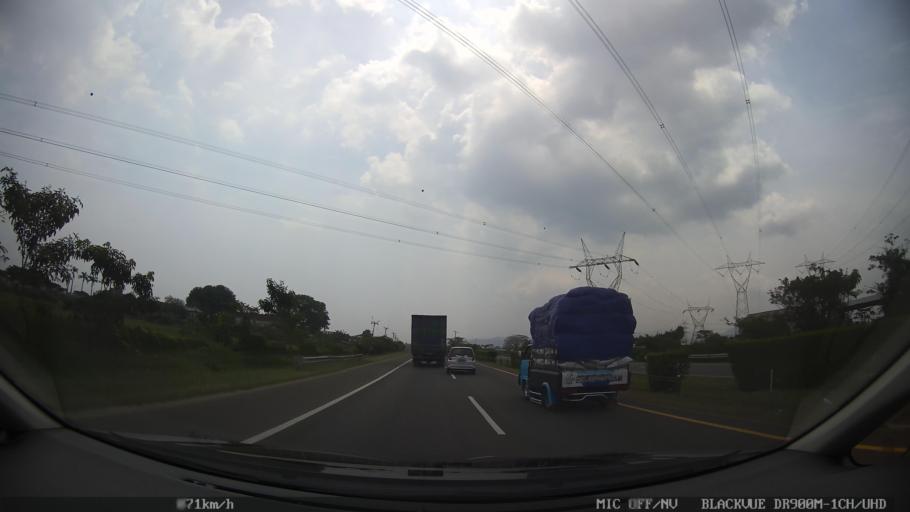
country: ID
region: Banten
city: Bojonegara
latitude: -6.0160
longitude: 106.0852
